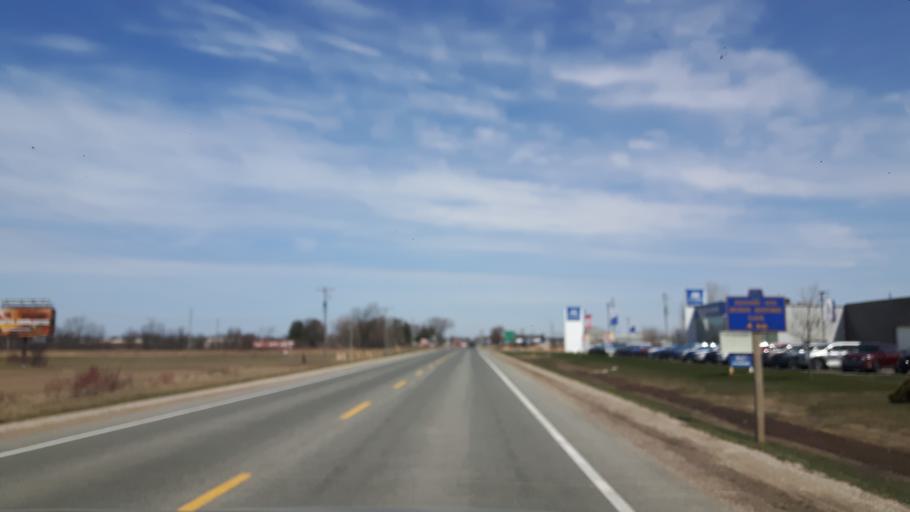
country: CA
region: Ontario
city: Goderich
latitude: 43.7211
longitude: -81.7058
